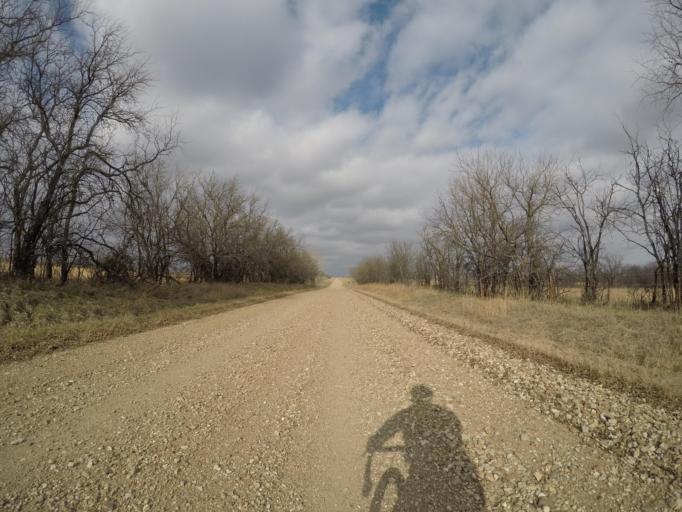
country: US
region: Kansas
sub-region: Morris County
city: Council Grove
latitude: 38.7857
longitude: -96.3527
